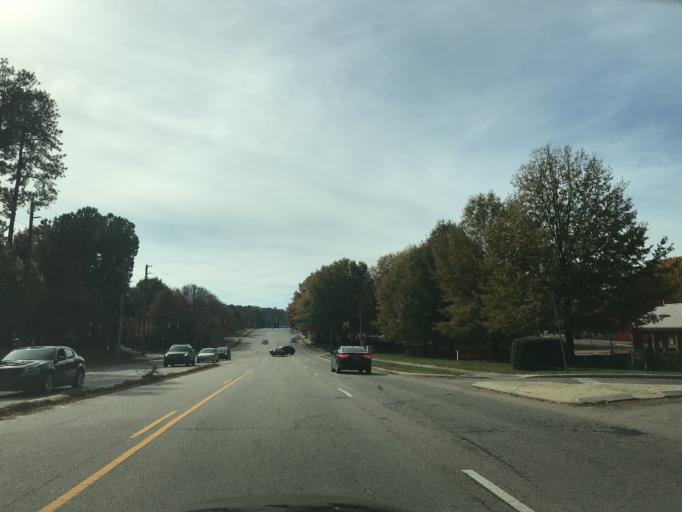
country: US
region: North Carolina
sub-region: Wake County
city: West Raleigh
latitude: 35.8269
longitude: -78.7042
